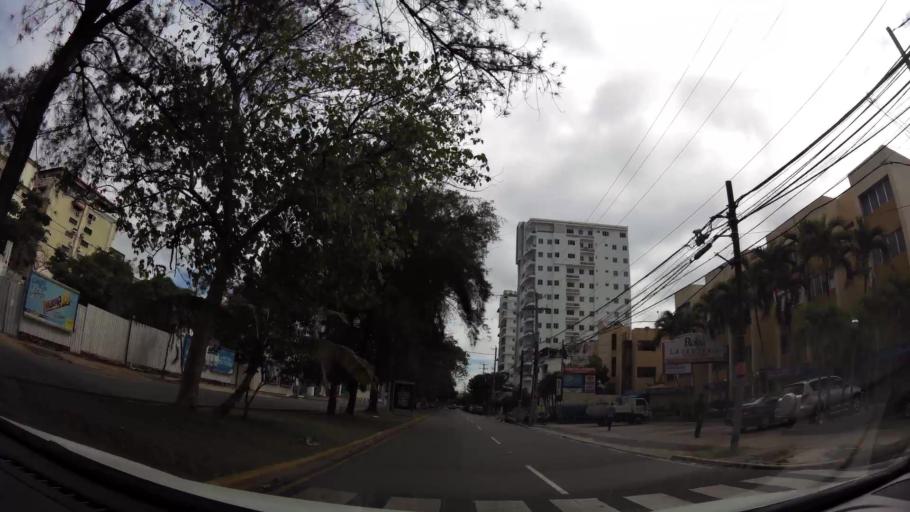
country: DO
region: Nacional
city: Bella Vista
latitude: 18.4505
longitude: -69.9485
